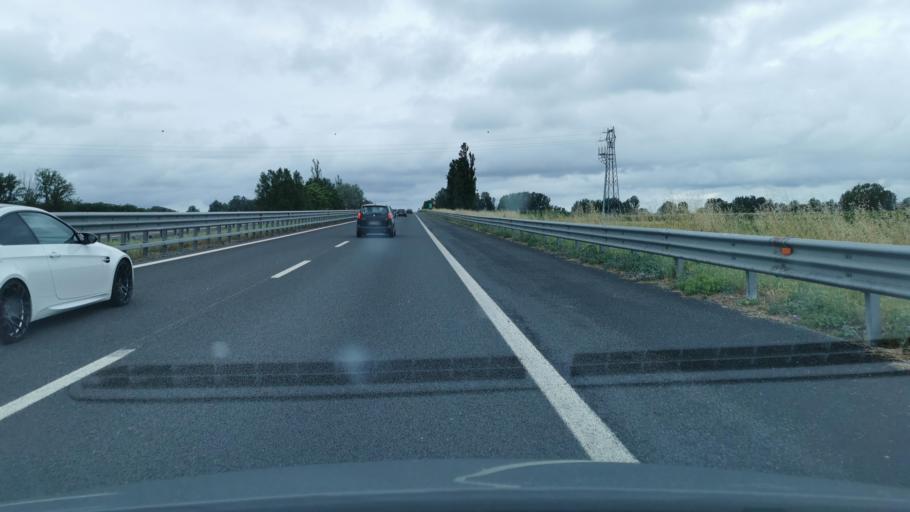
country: IT
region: Emilia-Romagna
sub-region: Provincia di Ravenna
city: Russi
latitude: 44.4049
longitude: 12.0323
